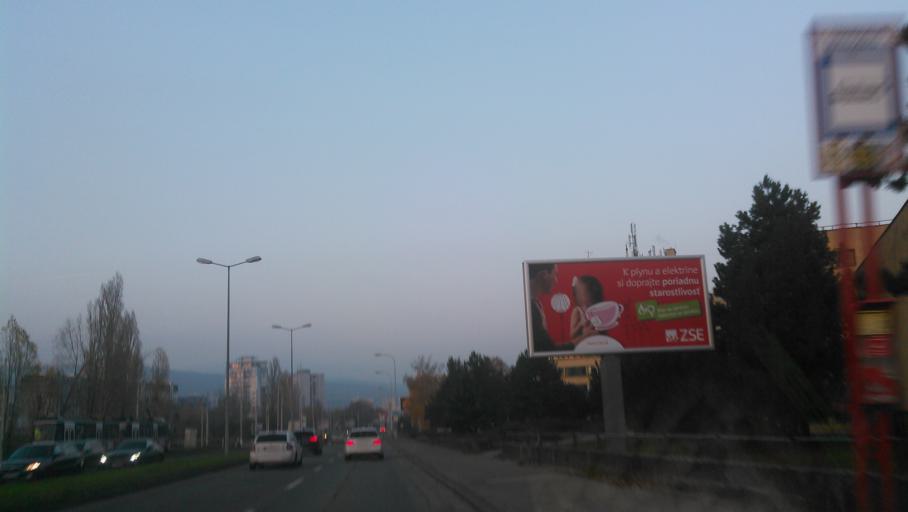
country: SK
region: Bratislavsky
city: Bratislava
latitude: 48.2002
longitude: 17.1482
